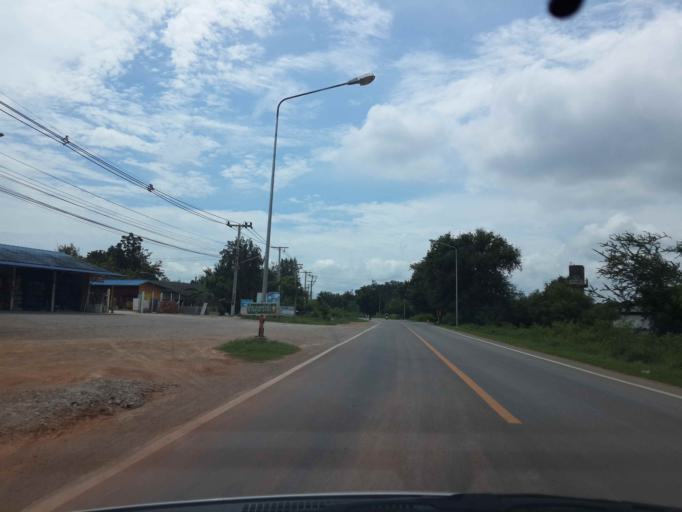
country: TH
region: Ratchaburi
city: Pak Tho
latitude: 13.3614
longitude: 99.7464
